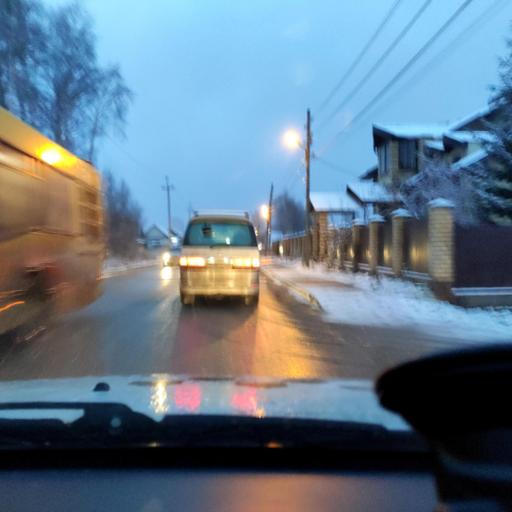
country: RU
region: Perm
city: Kondratovo
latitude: 58.0499
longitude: 56.0300
